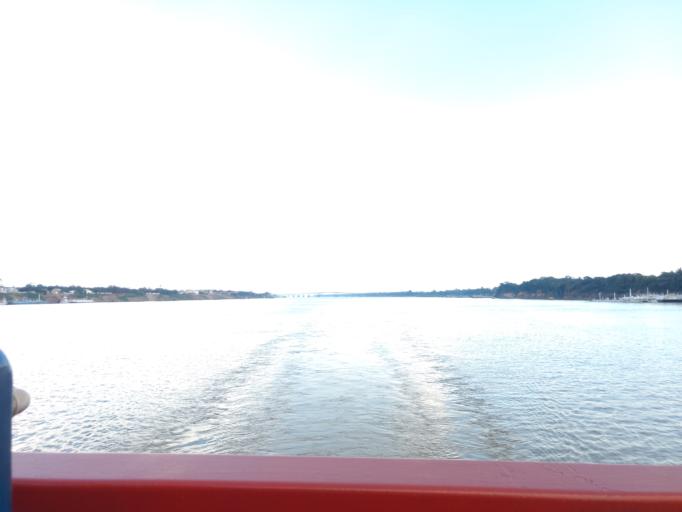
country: BR
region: Rondonia
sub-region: Porto Velho
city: Porto Velho
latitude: -8.6944
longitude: -63.9221
